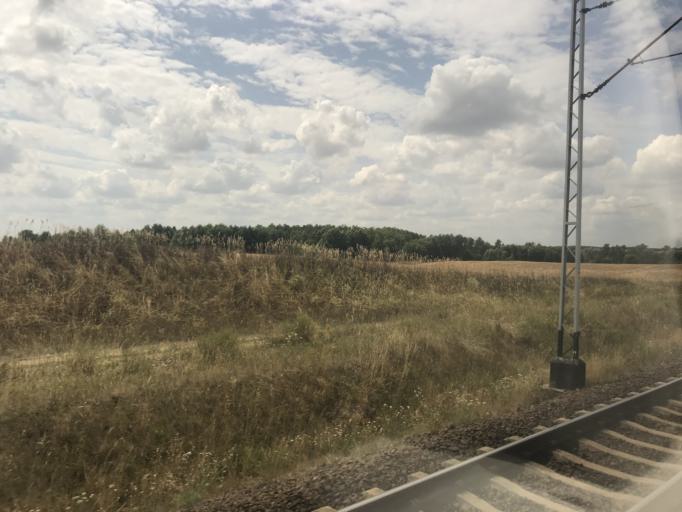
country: PL
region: Greater Poland Voivodeship
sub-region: Powiat poznanski
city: Buk
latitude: 52.3468
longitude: 16.5891
